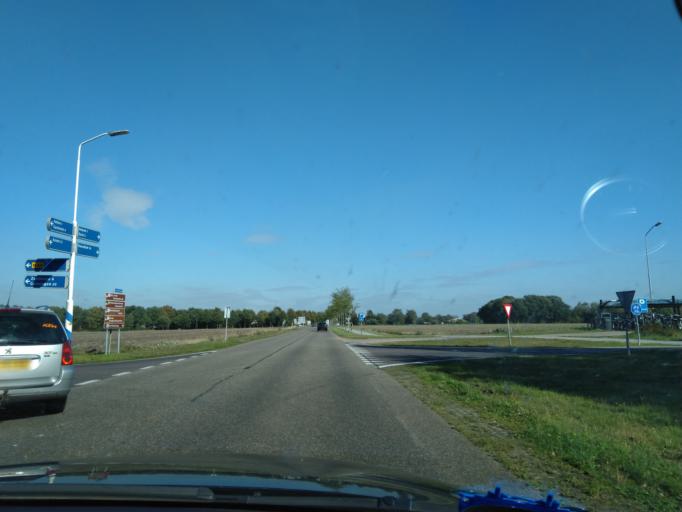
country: NL
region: Drenthe
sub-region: Gemeente Aa en Hunze
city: Anloo
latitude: 53.0488
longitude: 6.7136
